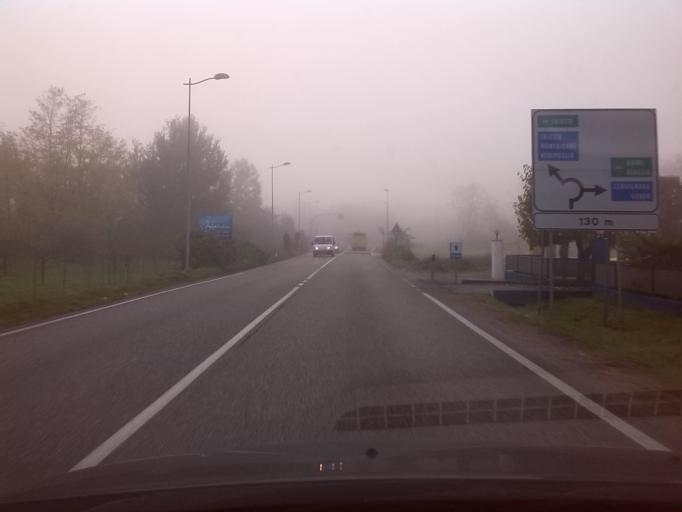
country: IT
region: Friuli Venezia Giulia
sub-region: Provincia di Gorizia
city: Sagrado
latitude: 45.8821
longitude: 13.4816
